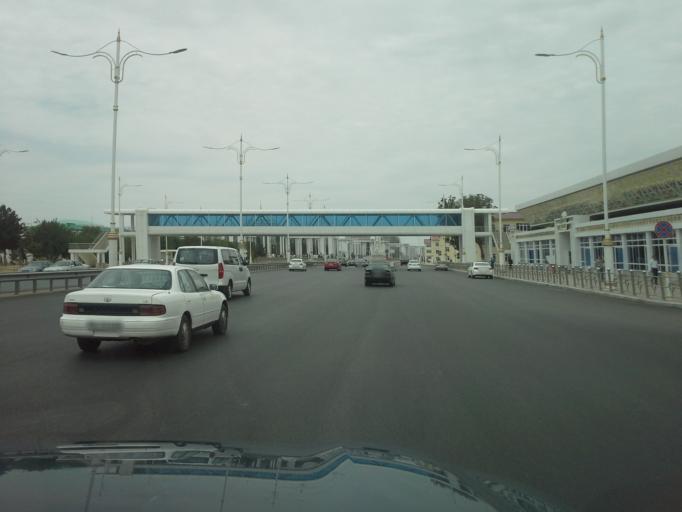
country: TM
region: Ahal
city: Ashgabat
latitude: 37.9254
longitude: 58.3908
